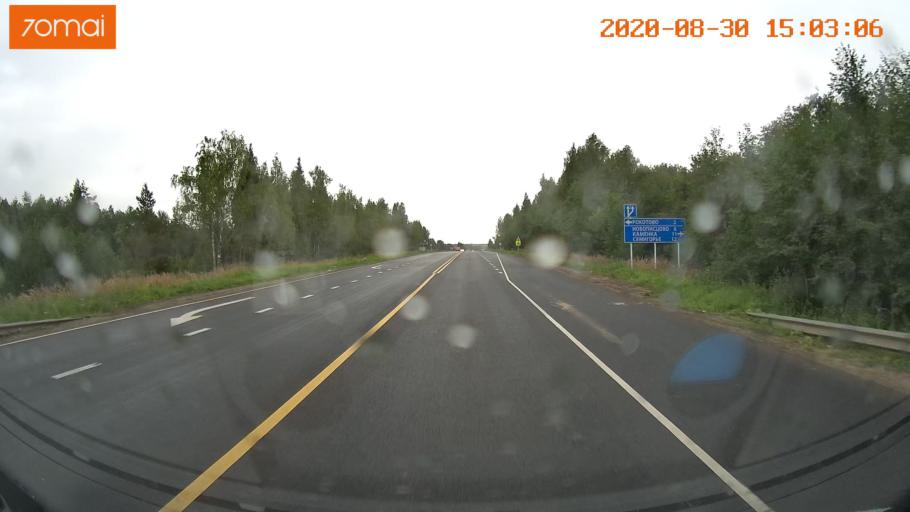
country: RU
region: Ivanovo
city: Staraya Vichuga
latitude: 57.3029
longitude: 41.9161
